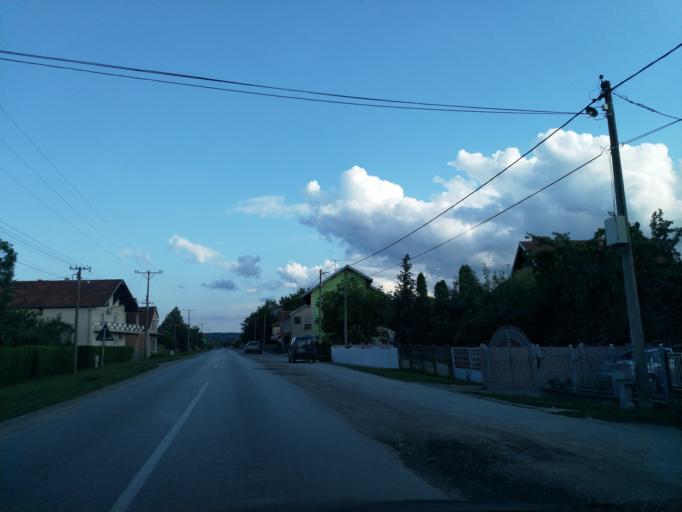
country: RS
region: Central Serbia
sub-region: Rasinski Okrug
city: Cicevac
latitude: 43.7637
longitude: 21.4298
